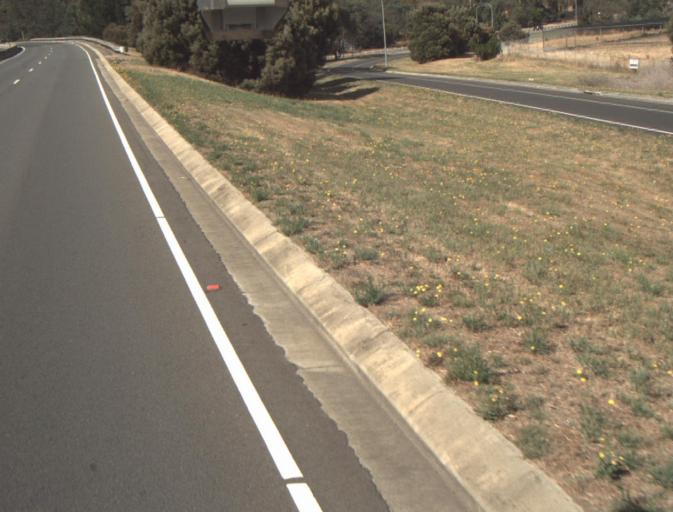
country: AU
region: Tasmania
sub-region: Launceston
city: Summerhill
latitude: -41.4704
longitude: 147.1427
